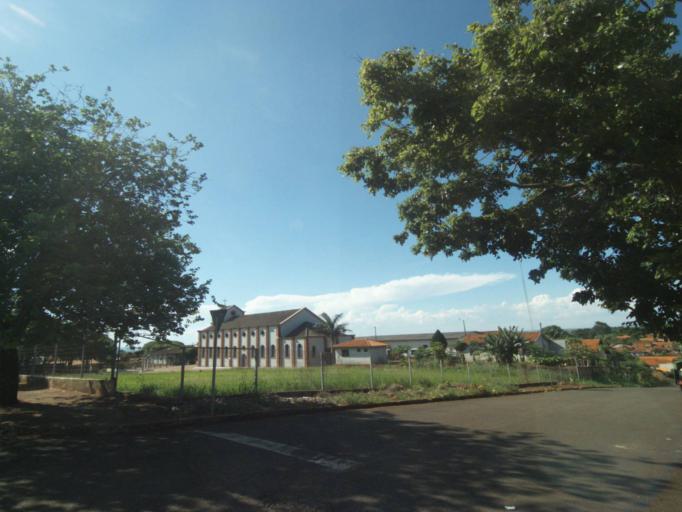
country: BR
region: Parana
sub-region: Sertanopolis
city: Sertanopolis
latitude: -23.0383
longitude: -50.8144
